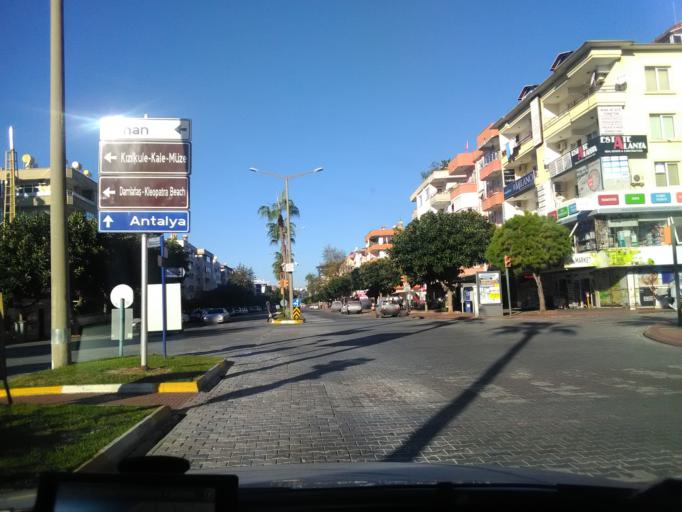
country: TR
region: Antalya
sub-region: Alanya
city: Alanya
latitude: 36.5465
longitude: 31.9888
